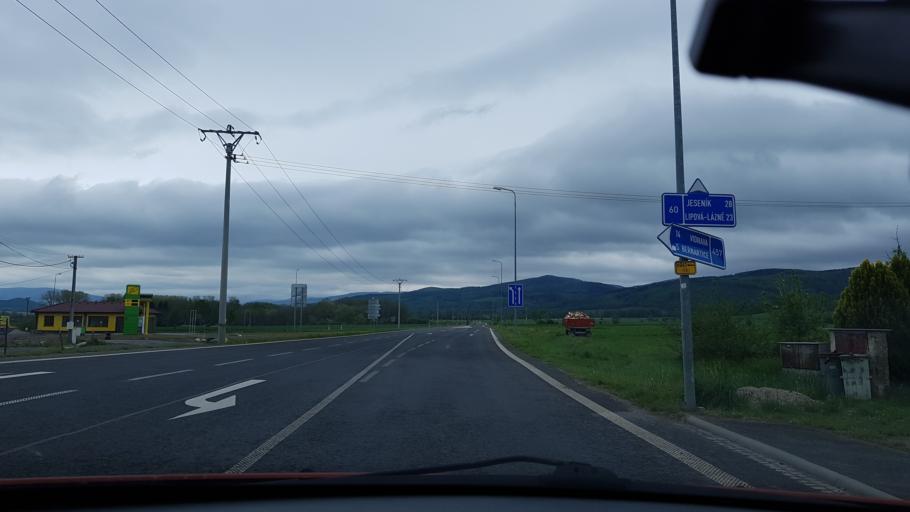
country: CZ
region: Olomoucky
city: Javornik
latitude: 50.3940
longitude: 17.0131
